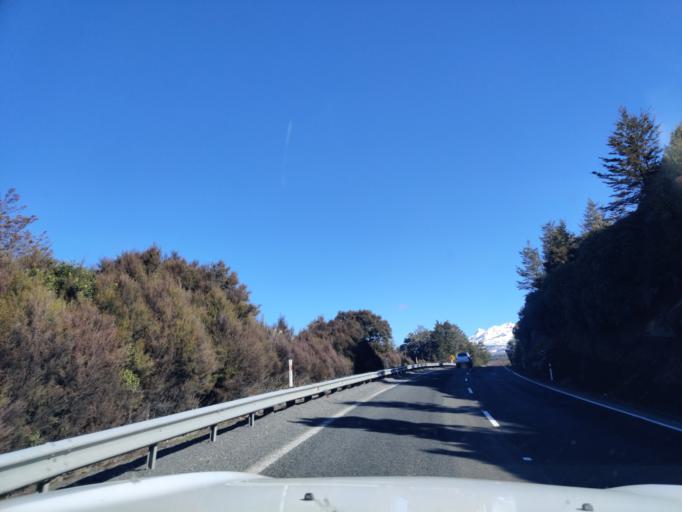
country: NZ
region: Waikato
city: Turangi
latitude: -39.2139
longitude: 175.7420
